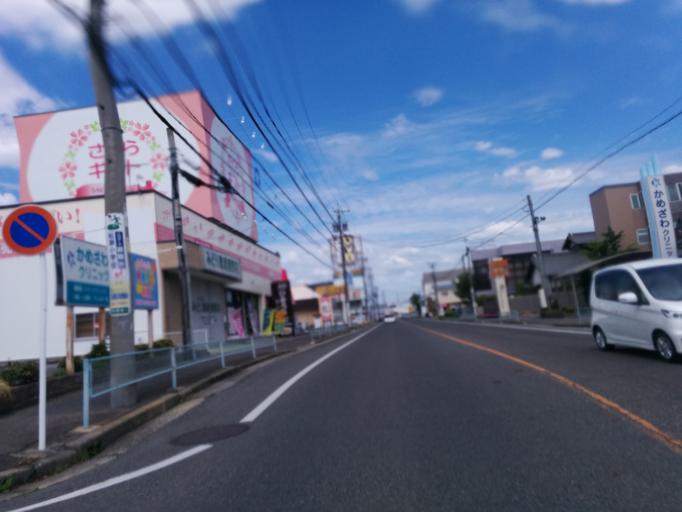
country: JP
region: Aichi
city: Kasugai
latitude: 35.2628
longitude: 136.9806
